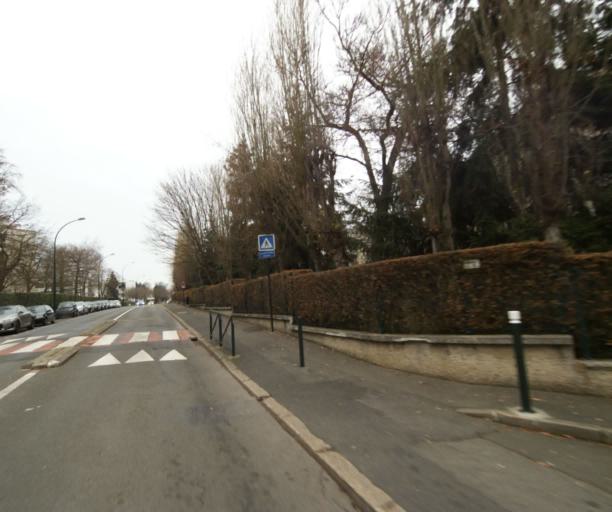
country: FR
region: Ile-de-France
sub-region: Departement des Hauts-de-Seine
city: Saint-Cloud
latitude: 48.8504
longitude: 2.1957
